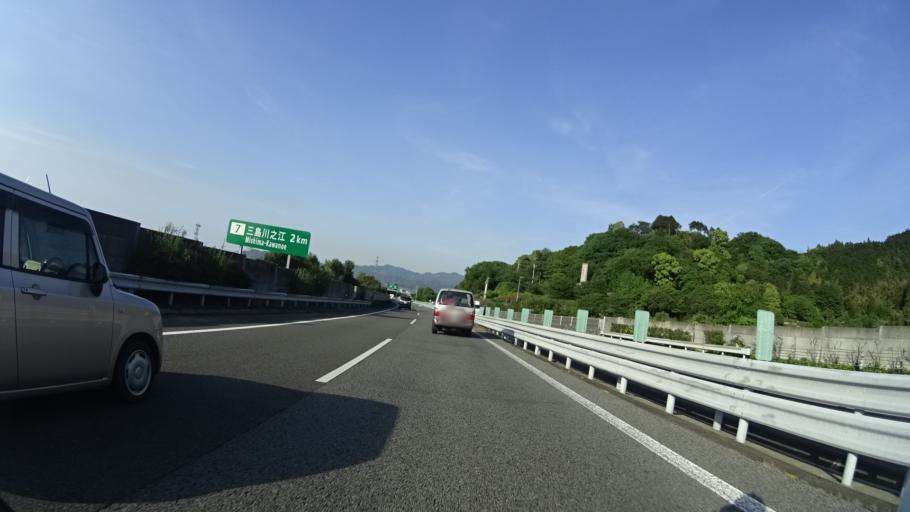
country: JP
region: Ehime
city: Kawanoecho
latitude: 33.9712
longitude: 133.5551
